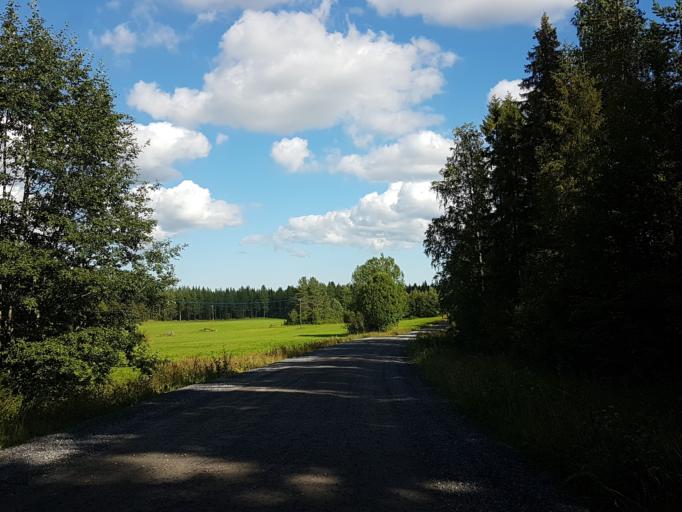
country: SE
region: Vaesterbotten
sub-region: Skelleftea Kommun
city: Burtraesk
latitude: 64.2944
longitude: 20.5144
